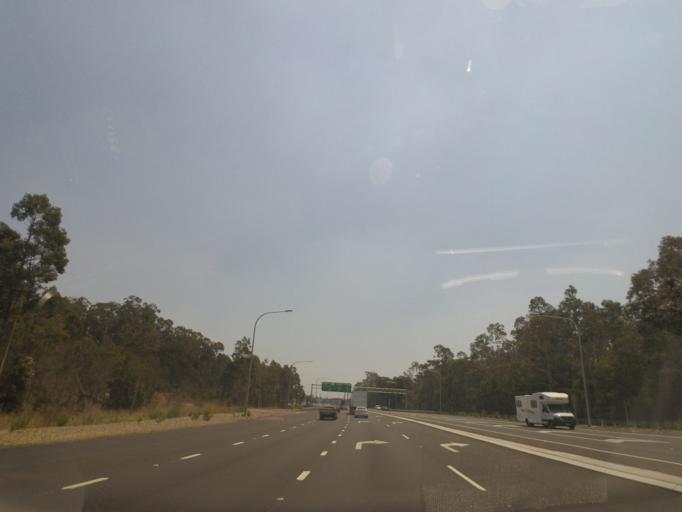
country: AU
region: New South Wales
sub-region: Newcastle
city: Beresfield
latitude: -32.8171
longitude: 151.6355
